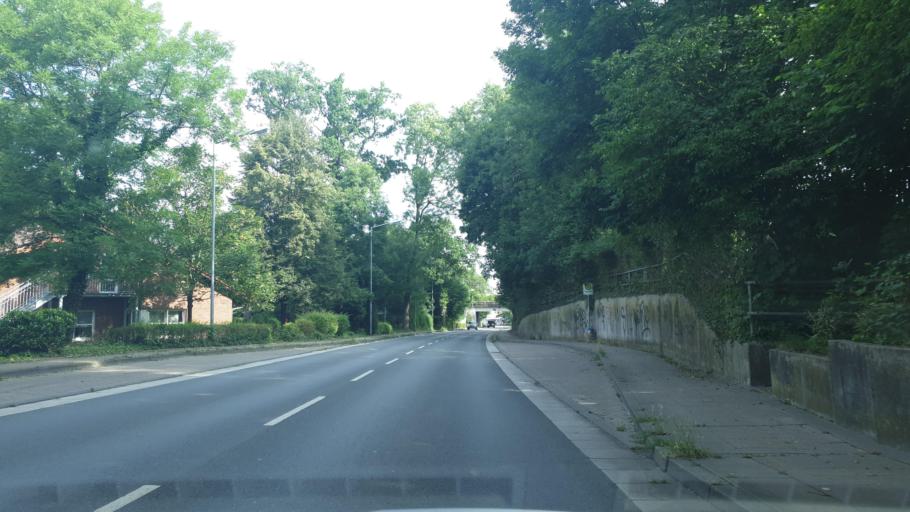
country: DE
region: North Rhine-Westphalia
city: Bad Oeynhausen
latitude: 52.1943
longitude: 8.7588
